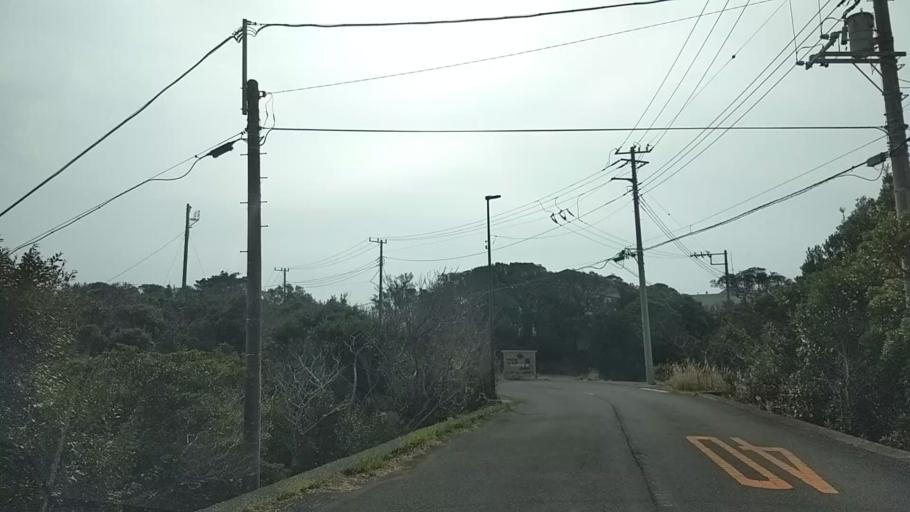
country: JP
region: Shizuoka
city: Shimoda
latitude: 34.6653
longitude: 138.9788
